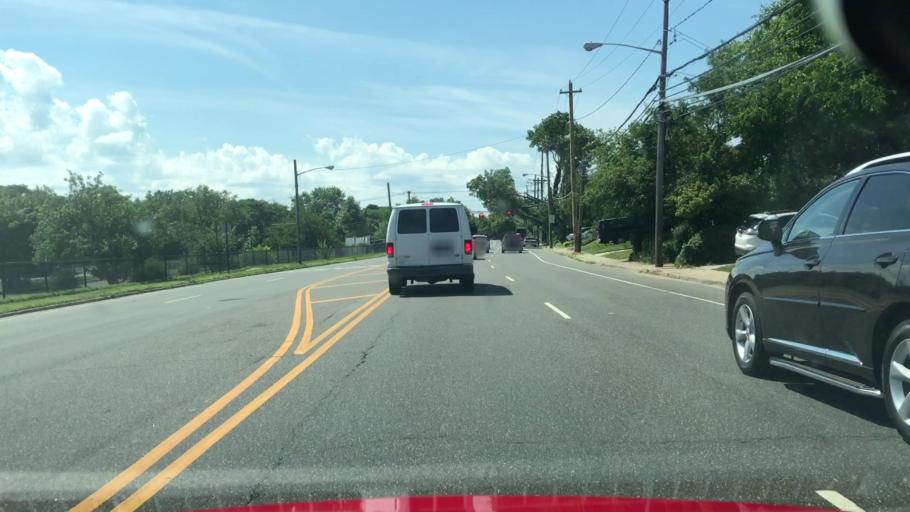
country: US
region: New York
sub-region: Nassau County
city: Malverne
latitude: 40.6687
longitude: -73.6611
